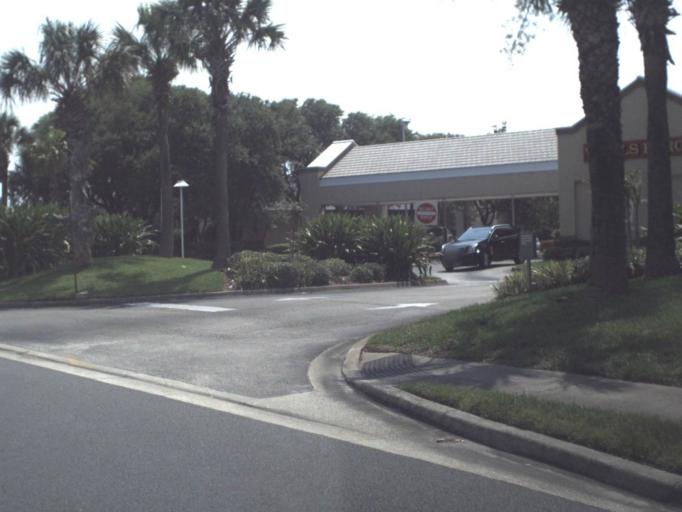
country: US
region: Florida
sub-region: Saint Johns County
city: Ponte Vedra Beach
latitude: 30.2594
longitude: -81.3874
